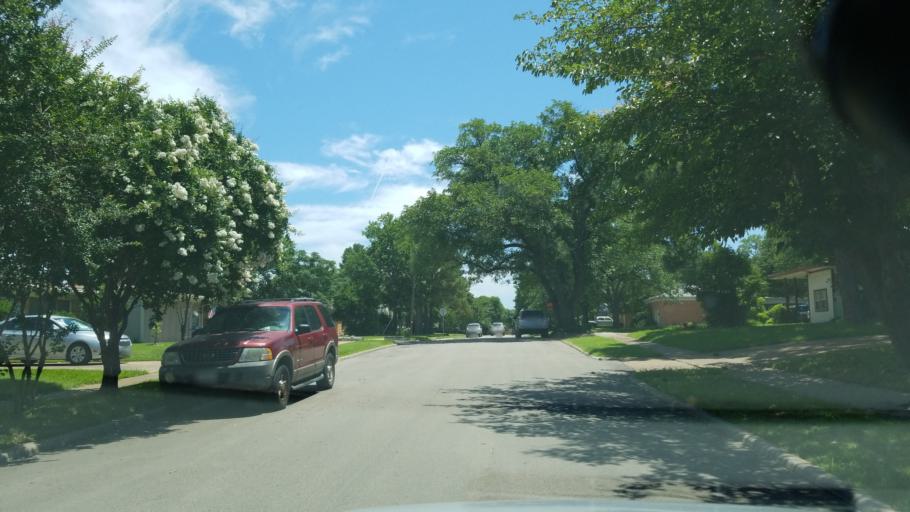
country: US
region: Texas
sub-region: Dallas County
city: Irving
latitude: 32.8323
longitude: -96.9727
